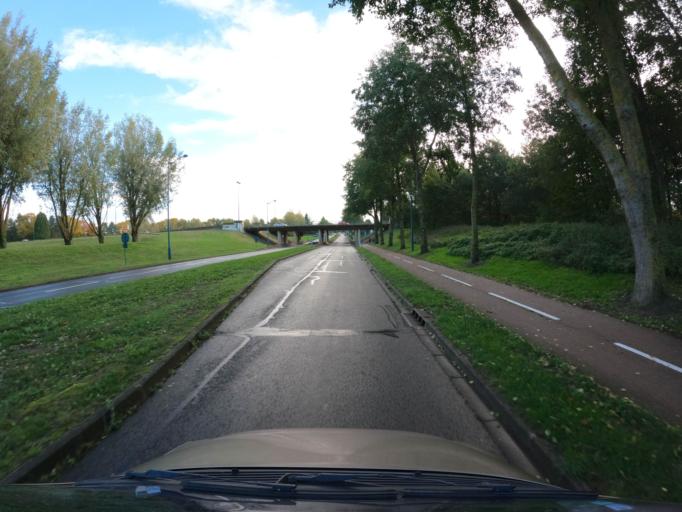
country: FR
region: Ile-de-France
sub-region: Departement de Seine-et-Marne
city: Bailly-Romainvilliers
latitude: 48.8472
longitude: 2.8080
